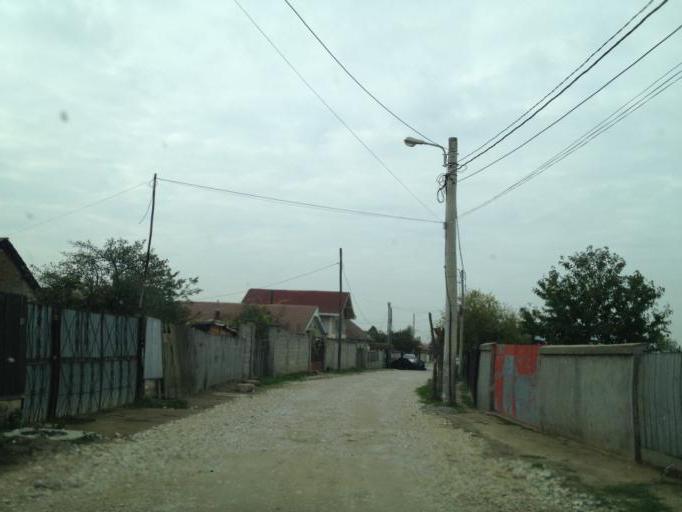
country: RO
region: Dolj
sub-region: Municipiul Craiova
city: Facai
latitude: 44.2863
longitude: 23.8069
